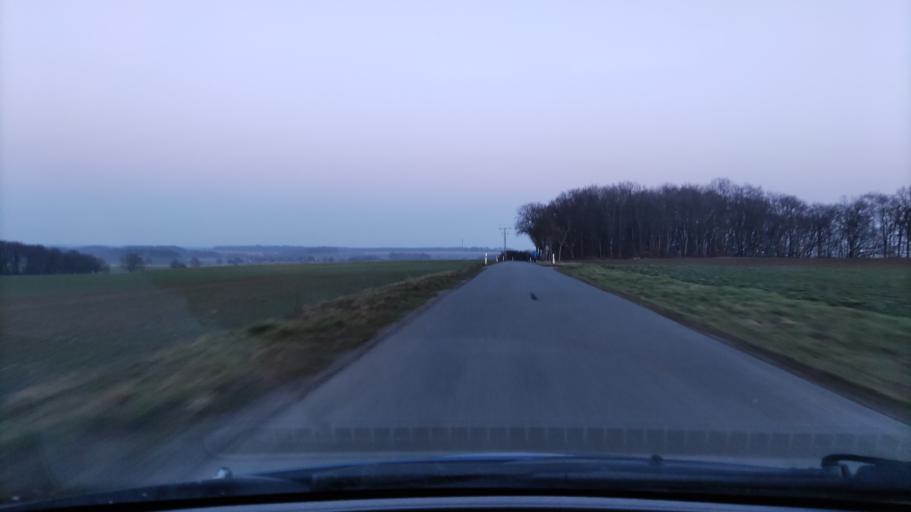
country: DE
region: Lower Saxony
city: Barum
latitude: 53.0545
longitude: 10.4944
